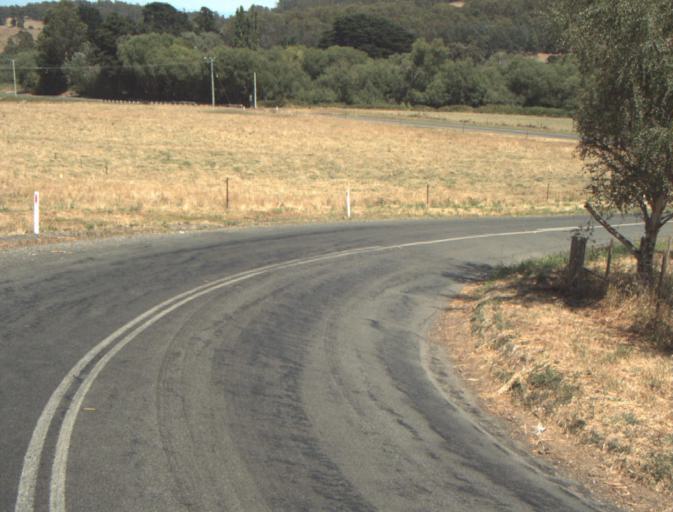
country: AU
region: Tasmania
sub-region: Launceston
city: Mayfield
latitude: -41.2589
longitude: 147.1373
